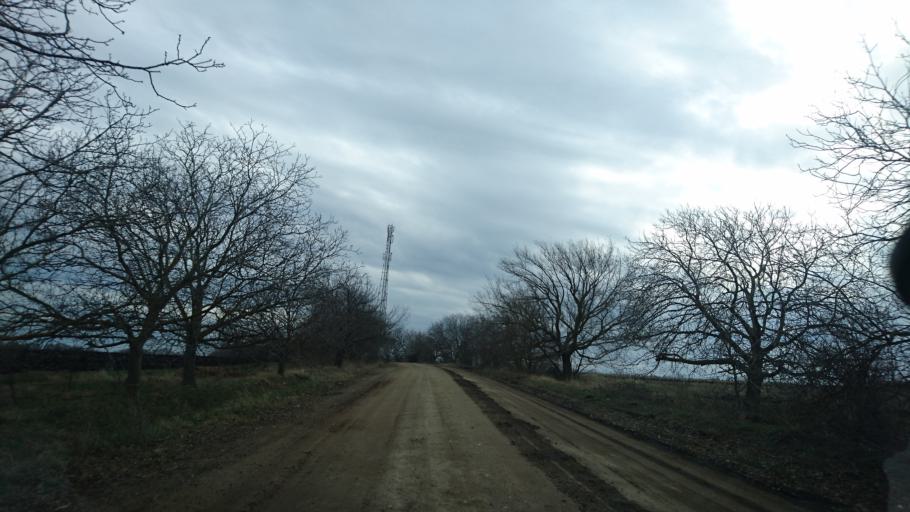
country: MD
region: Cantemir
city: Visniovca
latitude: 46.3027
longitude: 28.3995
